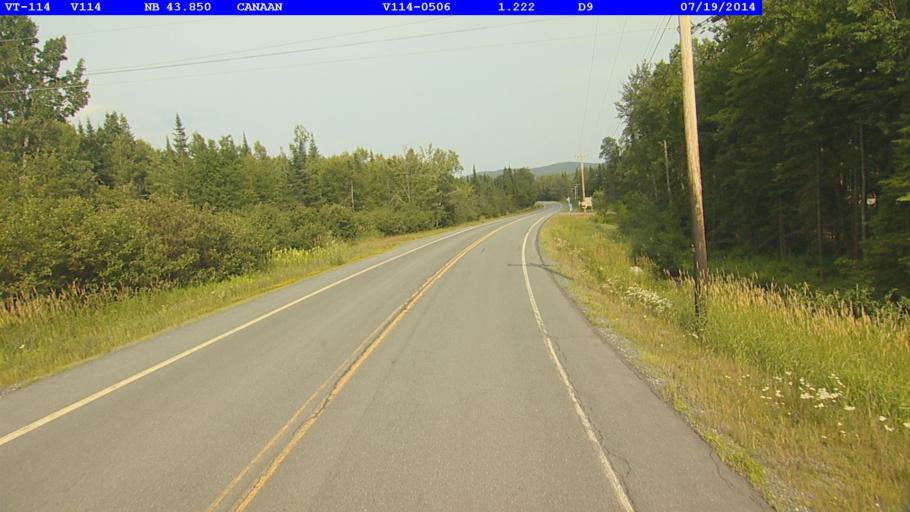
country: CA
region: Quebec
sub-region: Estrie
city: Coaticook
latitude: 45.0062
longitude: -71.6690
